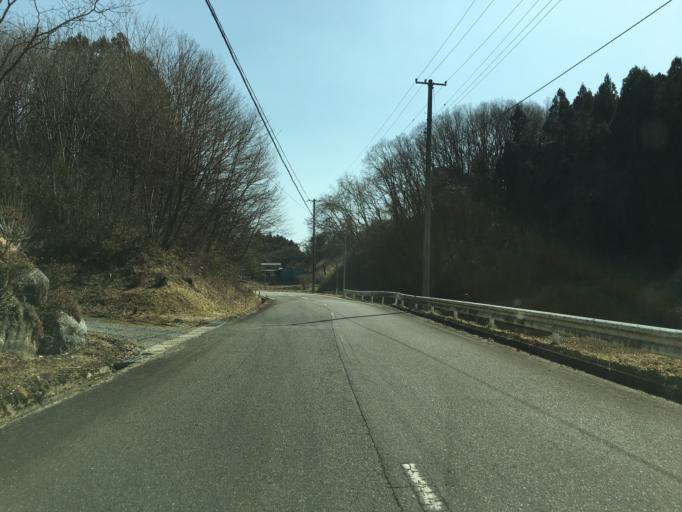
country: JP
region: Fukushima
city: Ishikawa
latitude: 37.0986
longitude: 140.4423
